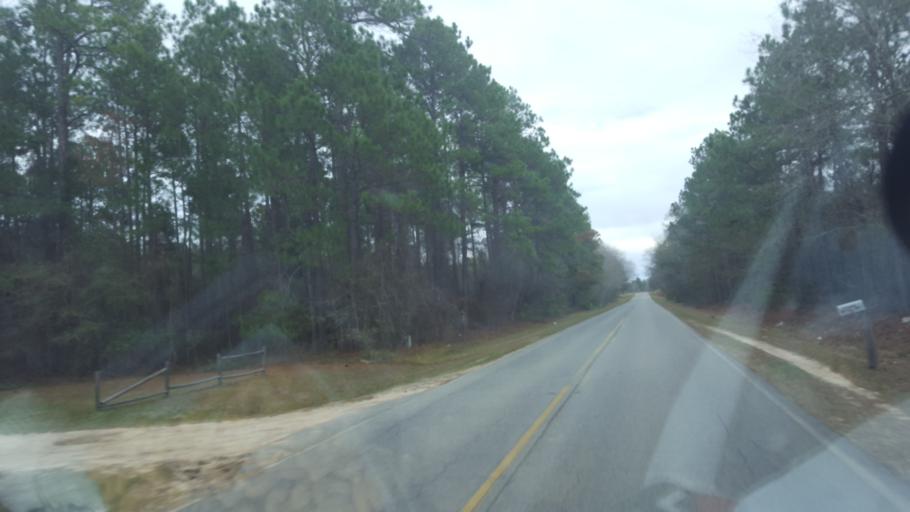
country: US
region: Georgia
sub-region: Ben Hill County
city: Fitzgerald
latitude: 31.7510
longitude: -83.3349
